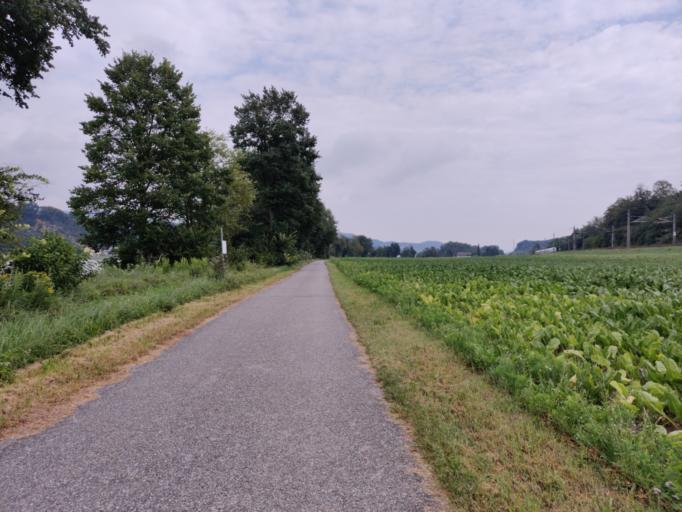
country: AT
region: Lower Austria
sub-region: Politischer Bezirk Melk
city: Marbach an der Donau
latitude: 48.2068
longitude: 15.1241
